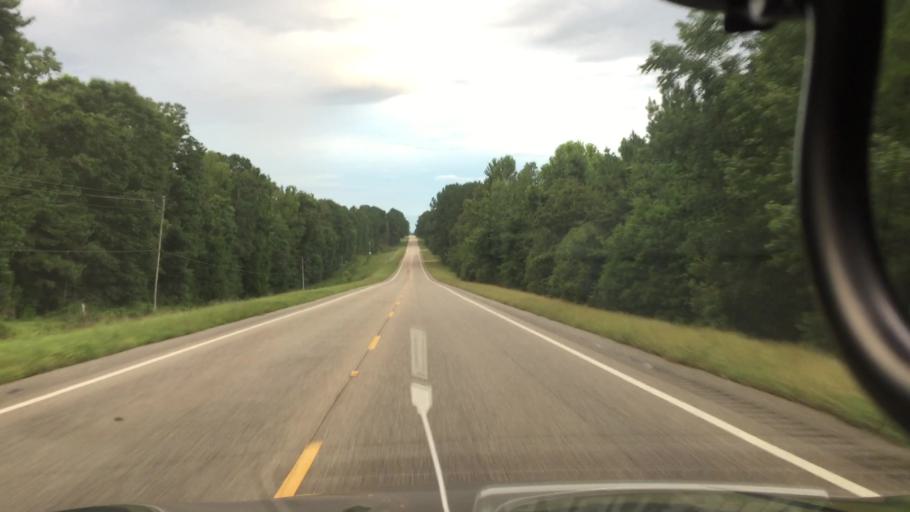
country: US
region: Alabama
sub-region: Pike County
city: Troy
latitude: 31.6703
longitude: -85.9552
